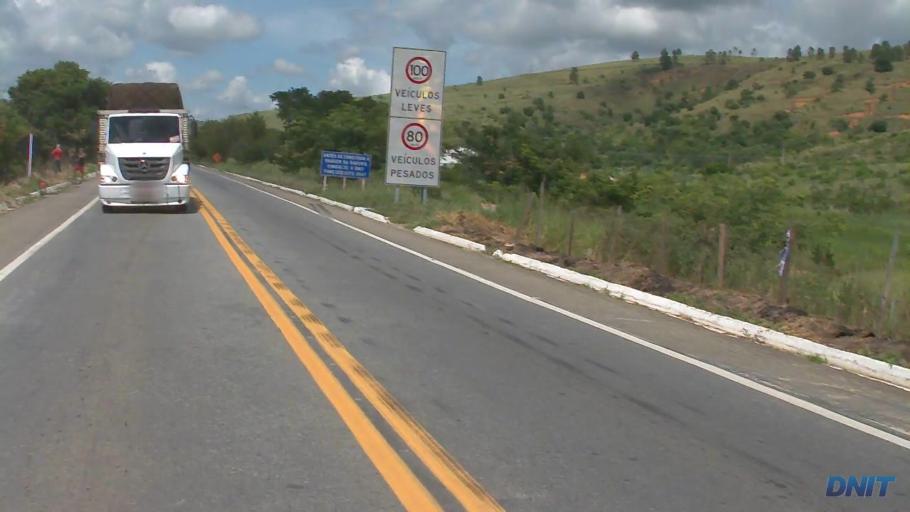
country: BR
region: Minas Gerais
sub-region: Governador Valadares
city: Governador Valadares
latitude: -18.9234
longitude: -42.0320
